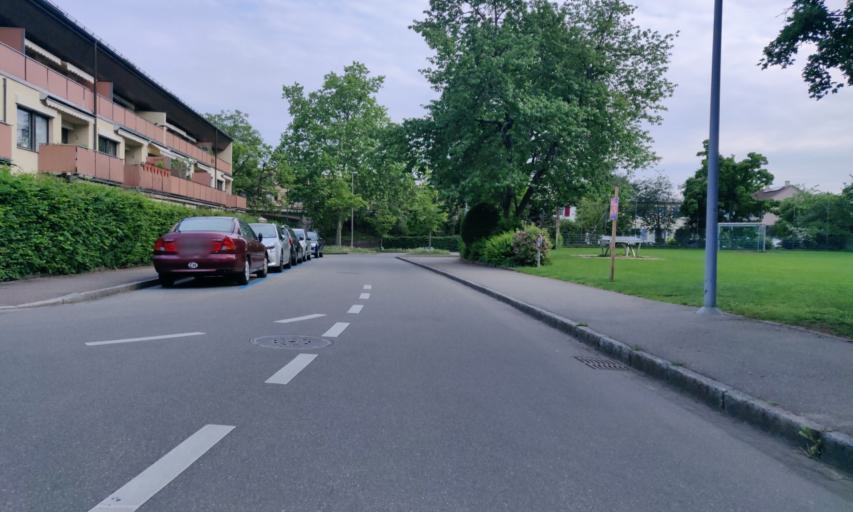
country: CH
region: Basel-City
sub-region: Basel-Stadt
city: Riehen
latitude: 47.5736
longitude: 7.6381
